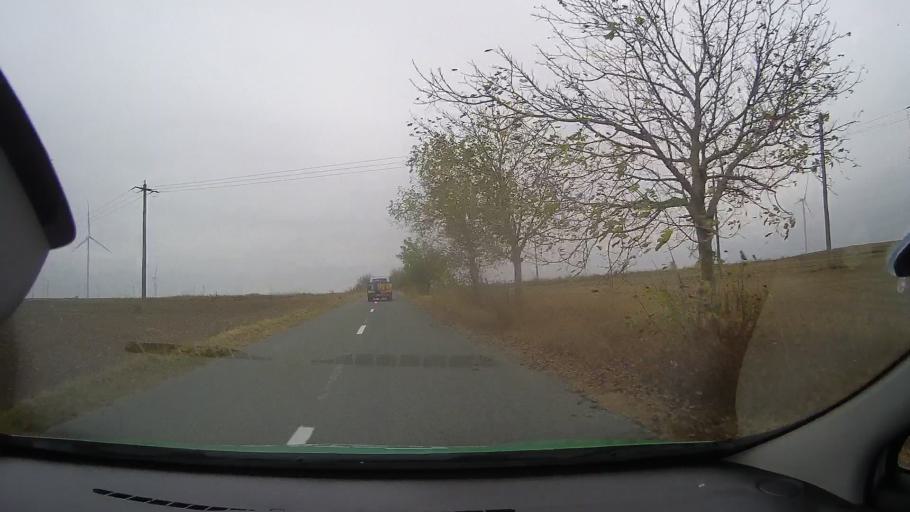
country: RO
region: Constanta
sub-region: Comuna Targusor
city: Targusor
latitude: 44.4794
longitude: 28.3751
